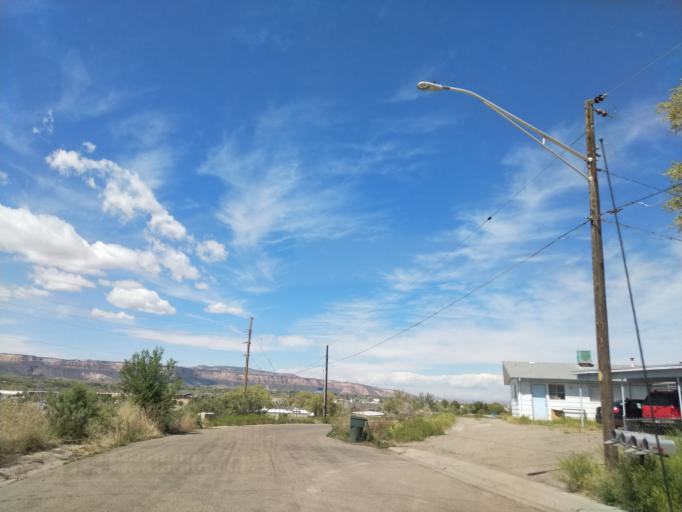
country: US
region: Colorado
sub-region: Mesa County
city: Grand Junction
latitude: 39.0792
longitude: -108.5749
